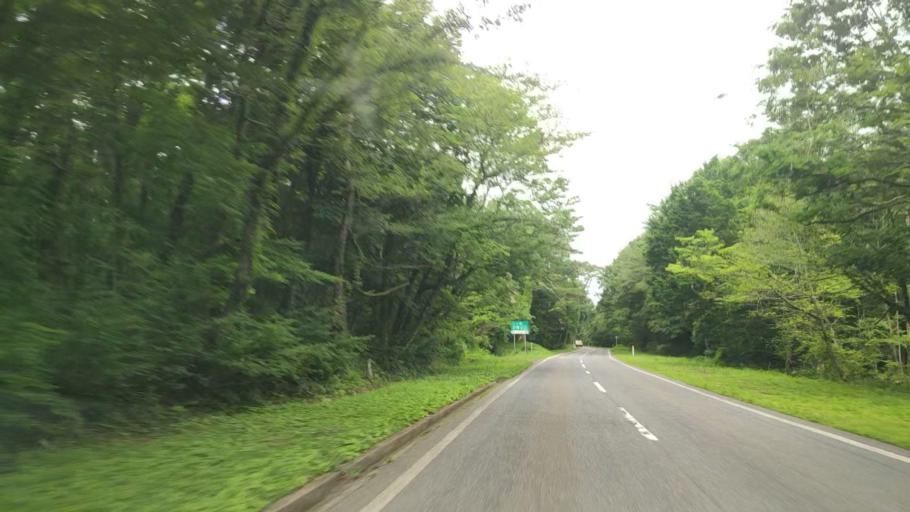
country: JP
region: Tottori
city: Yonago
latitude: 35.3988
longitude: 133.5055
